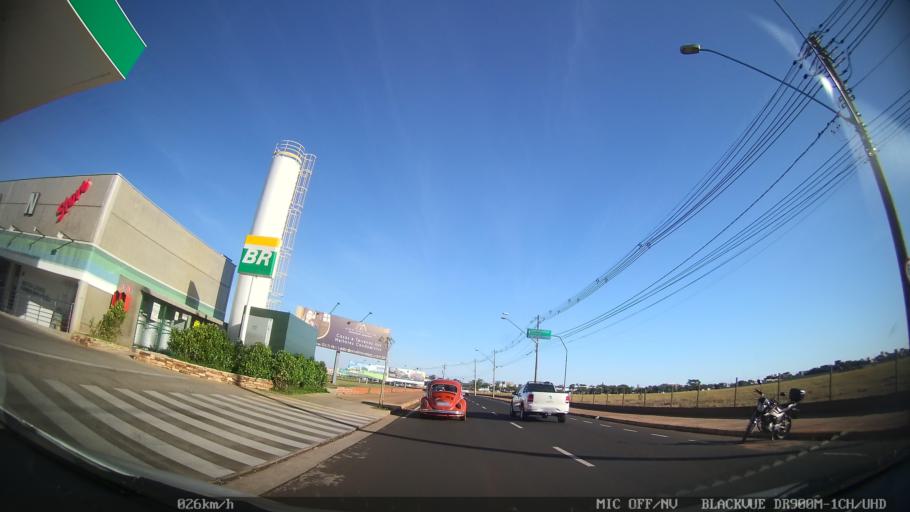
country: BR
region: Sao Paulo
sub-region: Sao Jose Do Rio Preto
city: Sao Jose do Rio Preto
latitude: -20.8511
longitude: -49.4133
